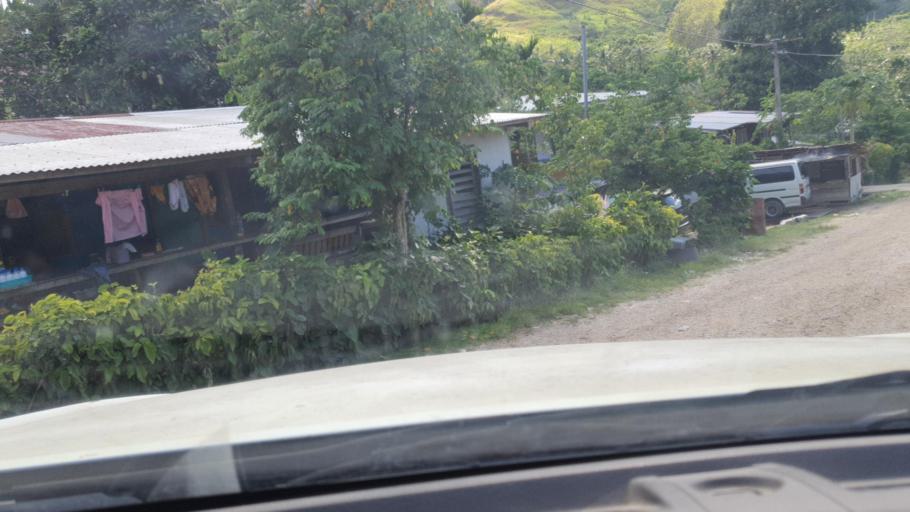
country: SB
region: Guadalcanal
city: Honiara
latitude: -9.4556
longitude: 159.9572
